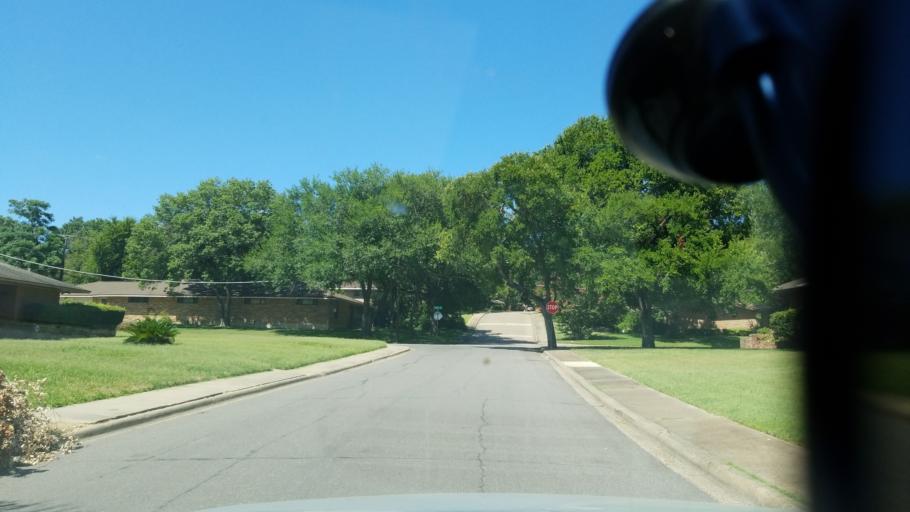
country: US
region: Texas
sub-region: Dallas County
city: Cockrell Hill
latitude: 32.6858
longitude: -96.8346
